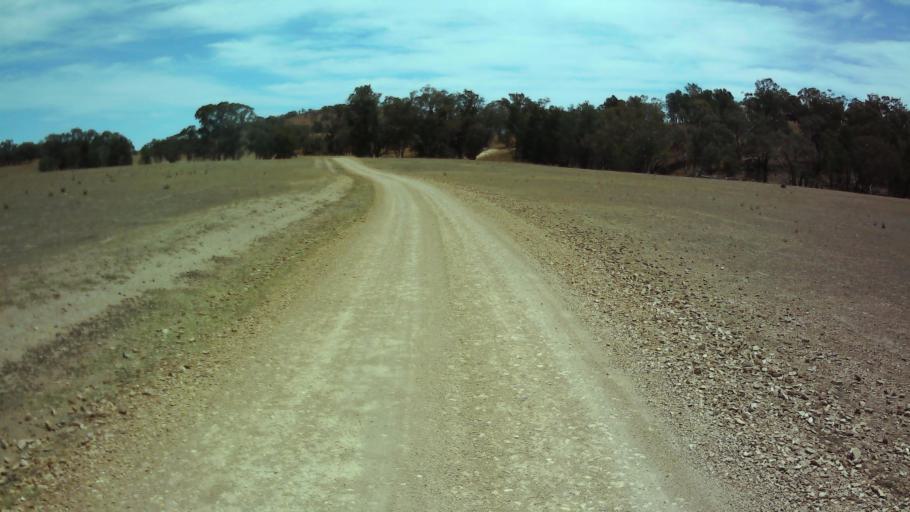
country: AU
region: New South Wales
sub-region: Weddin
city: Grenfell
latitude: -33.7425
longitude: 148.1754
